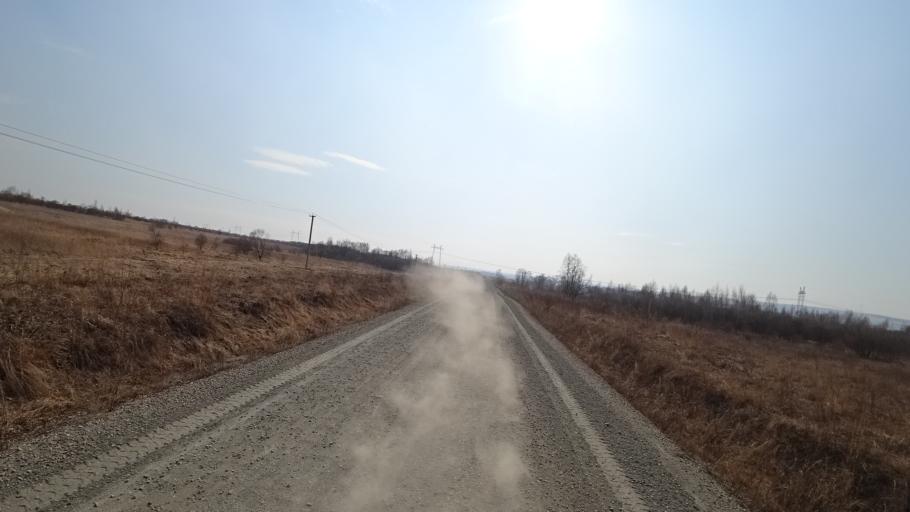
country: RU
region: Amur
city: Novobureyskiy
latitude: 49.8178
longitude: 129.9785
